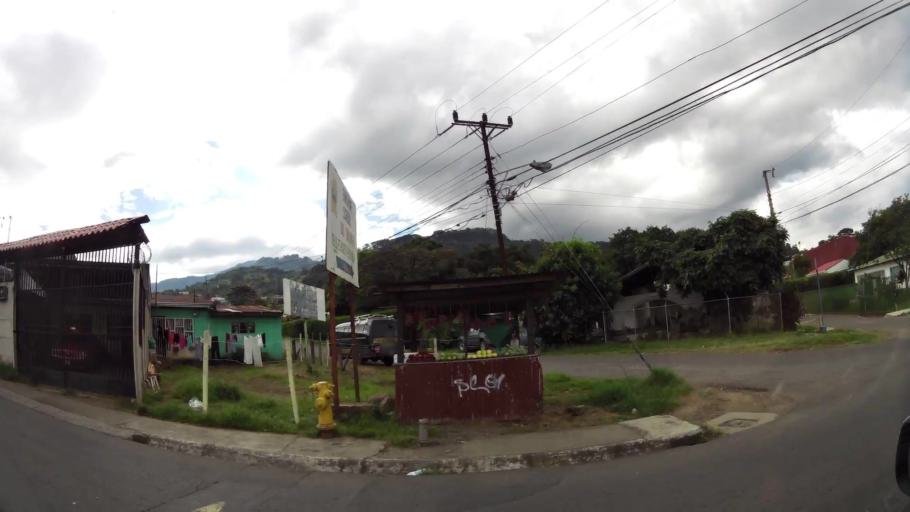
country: CR
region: San Jose
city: San Juan de Dios
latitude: 9.8821
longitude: -84.0843
